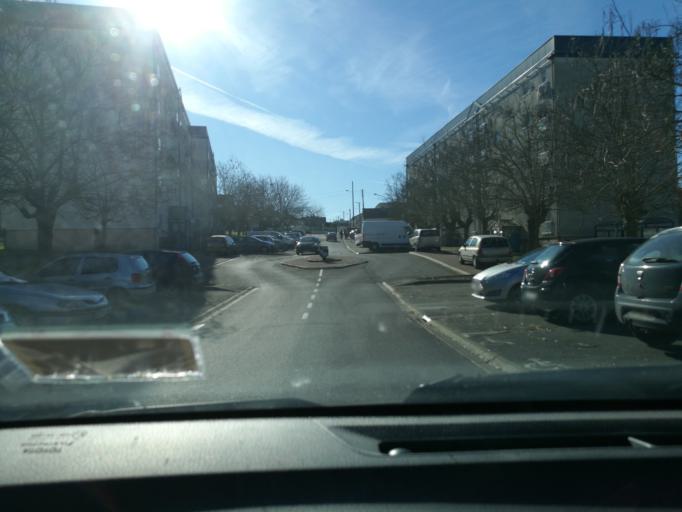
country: FR
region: Centre
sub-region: Departement du Loiret
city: Saint-Jean-de-la-Ruelle
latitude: 47.9042
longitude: 1.8762
